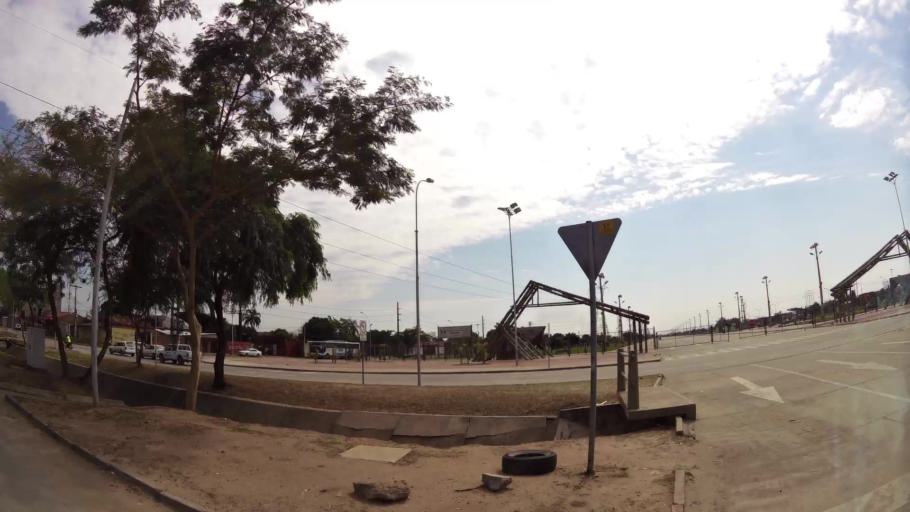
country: BO
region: Santa Cruz
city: Santa Cruz de la Sierra
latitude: -17.7488
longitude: -63.1502
